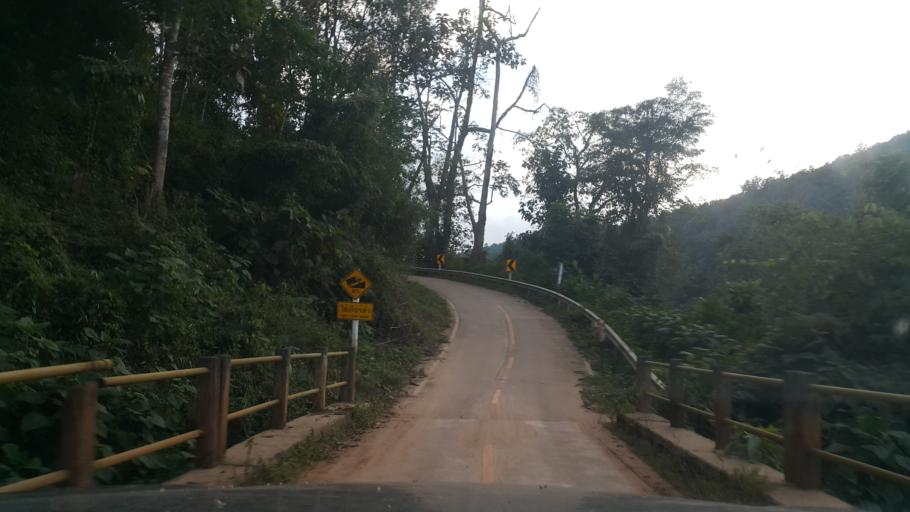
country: TH
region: Chiang Mai
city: Samoeng
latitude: 18.9957
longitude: 98.6735
